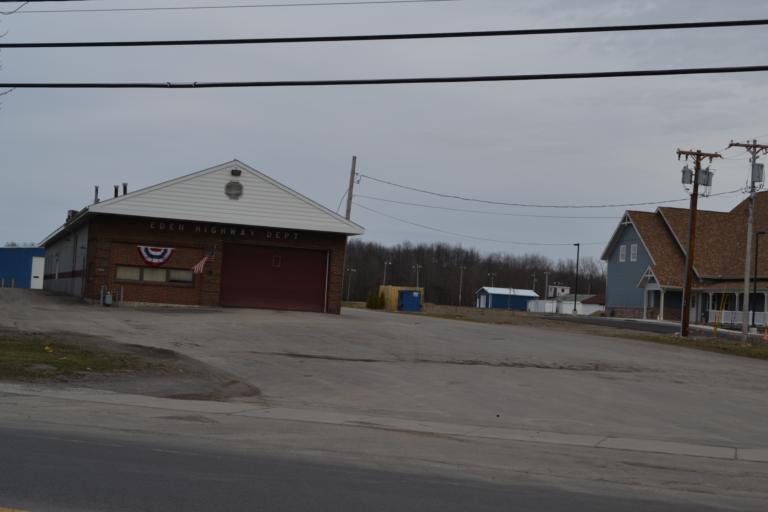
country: US
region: New York
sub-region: Erie County
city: Eden
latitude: 42.6640
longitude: -78.8901
